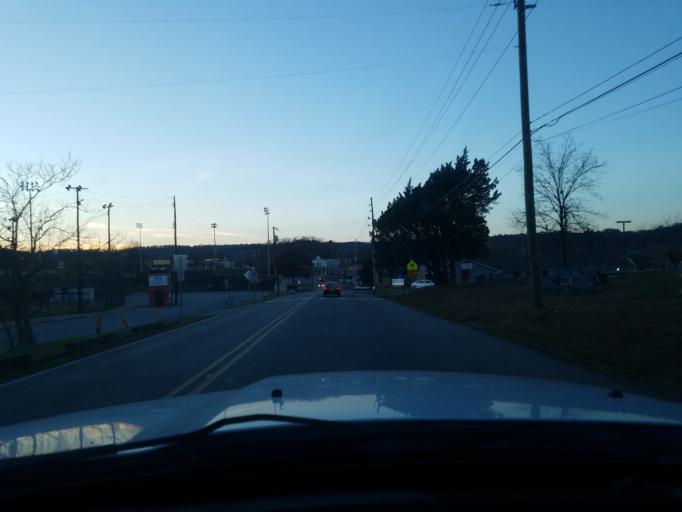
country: US
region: Indiana
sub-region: Floyd County
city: New Albany
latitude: 38.3313
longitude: -85.8151
